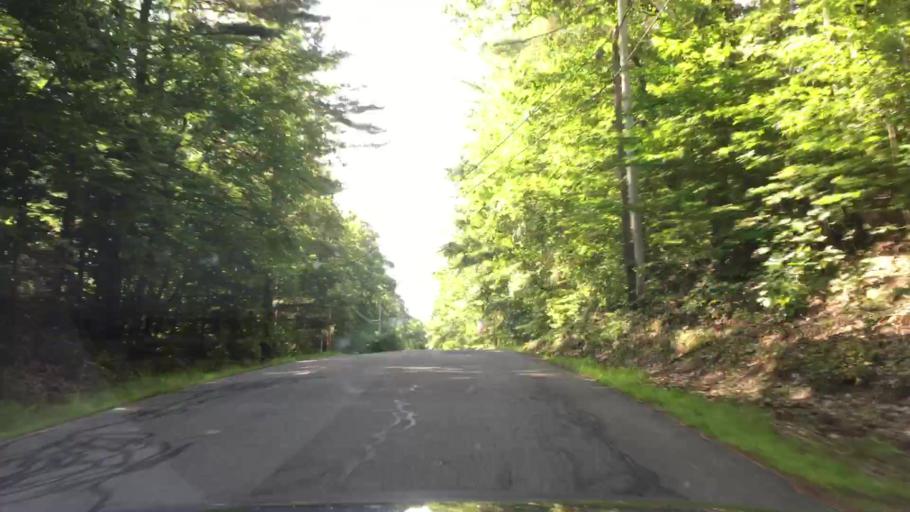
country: US
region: New Hampshire
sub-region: Grafton County
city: Ashland
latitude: 43.7183
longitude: -71.6281
